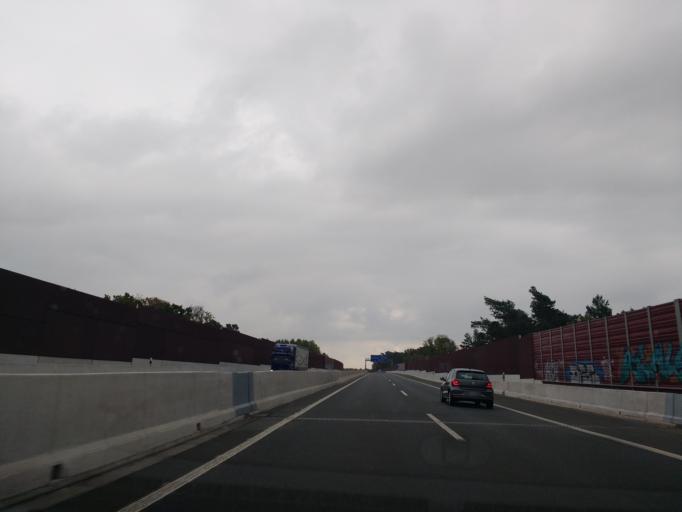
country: DE
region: North Rhine-Westphalia
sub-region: Regierungsbezirk Detmold
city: Steinhagen
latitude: 51.9814
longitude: 8.4614
